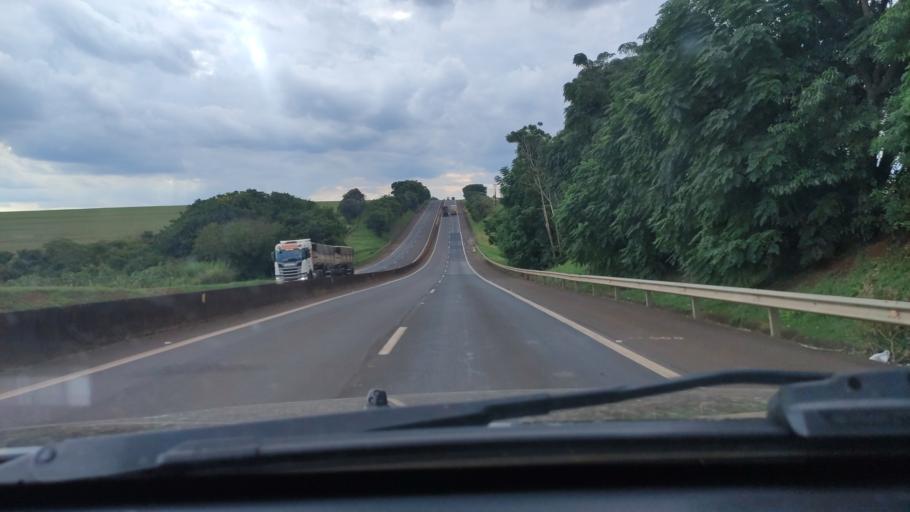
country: BR
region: Sao Paulo
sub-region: Ourinhos
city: Ourinhos
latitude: -22.8420
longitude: -50.0138
